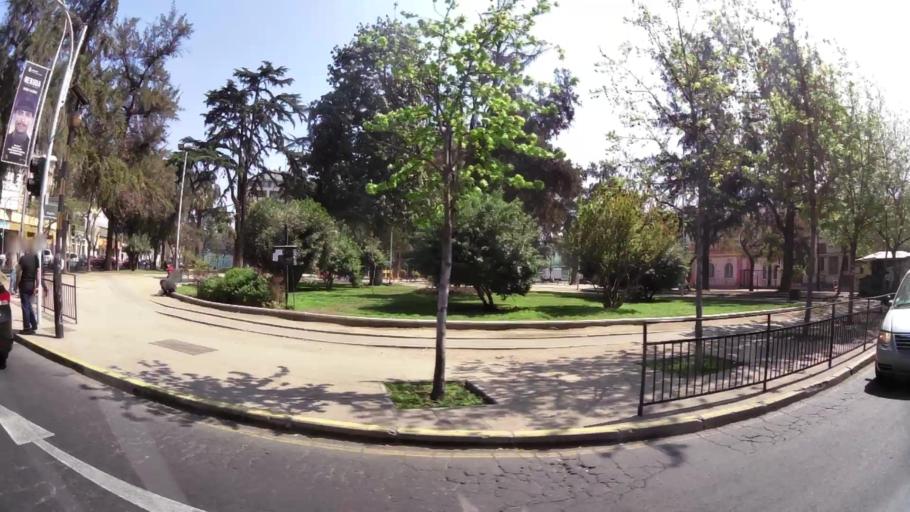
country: CL
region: Santiago Metropolitan
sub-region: Provincia de Santiago
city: Santiago
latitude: -33.4515
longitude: -70.6647
